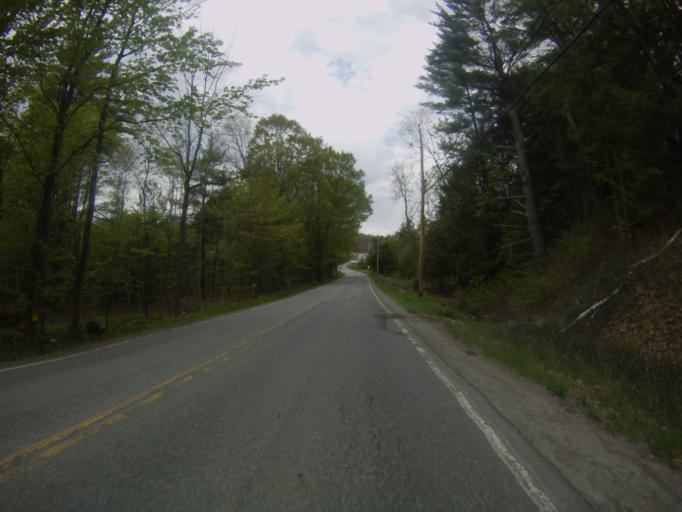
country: US
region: New York
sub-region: Essex County
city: Port Henry
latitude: 43.9581
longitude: -73.4874
